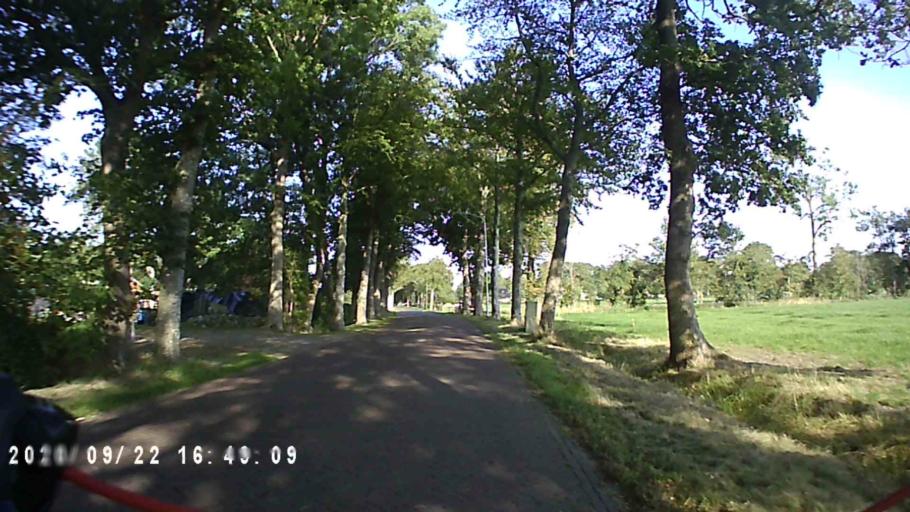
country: NL
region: Groningen
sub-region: Gemeente Leek
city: Leek
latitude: 53.1354
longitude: 6.4831
